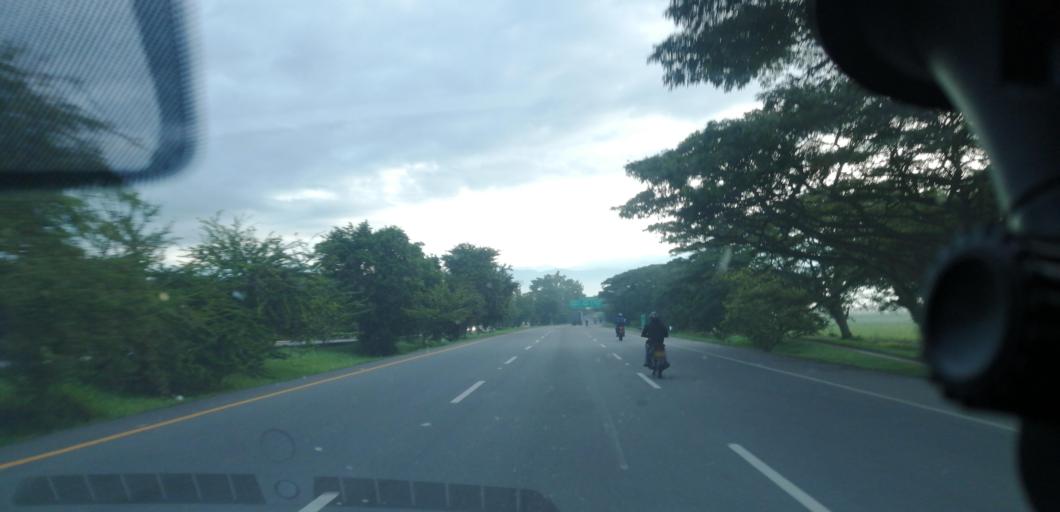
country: CO
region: Valle del Cauca
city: Palmira
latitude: 3.5225
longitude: -76.3471
